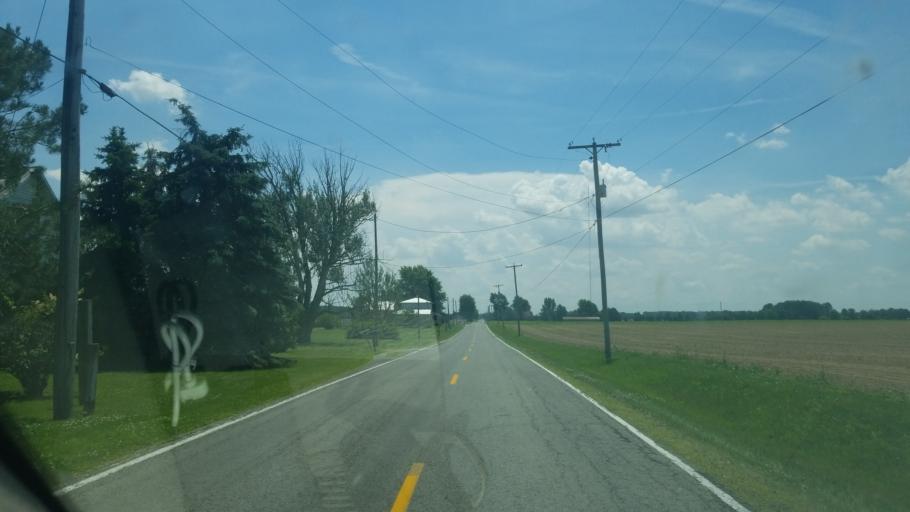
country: US
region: Ohio
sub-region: Hancock County
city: Arlington
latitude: 40.9232
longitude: -83.5946
